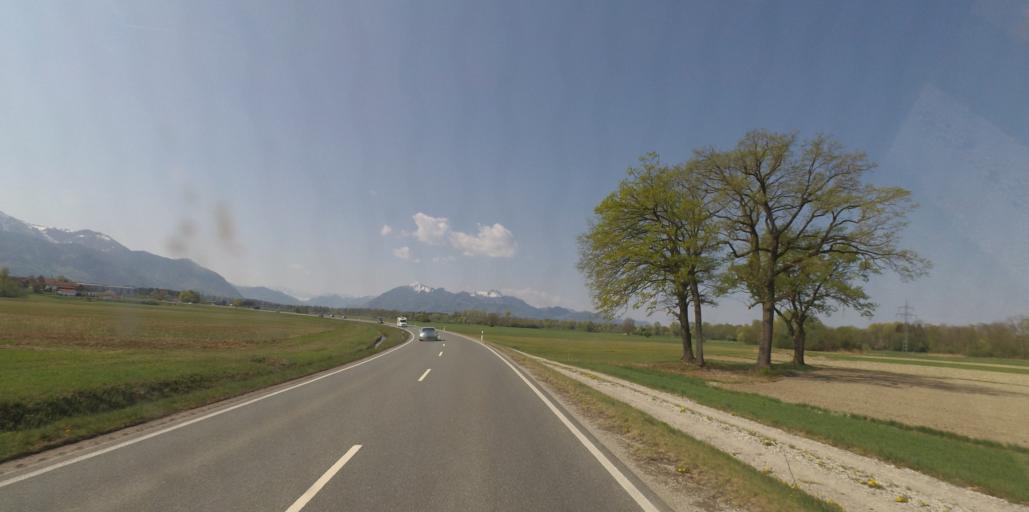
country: DE
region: Bavaria
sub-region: Upper Bavaria
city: Grabenstatt
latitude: 47.8367
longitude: 12.5266
